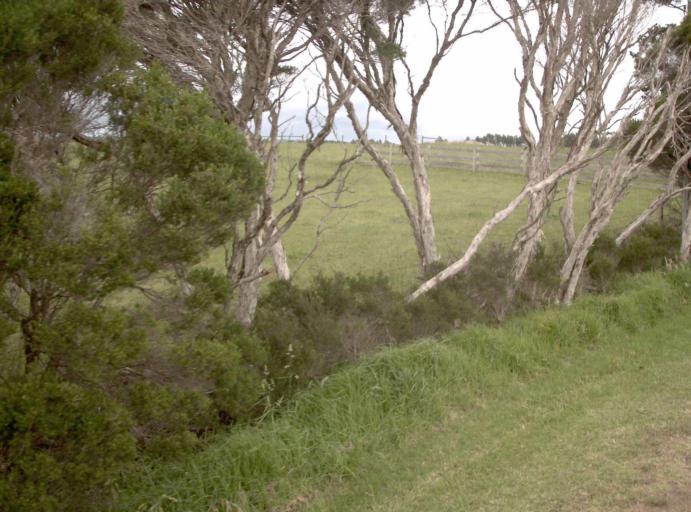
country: AU
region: Victoria
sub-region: Bass Coast
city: North Wonthaggi
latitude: -38.5511
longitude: 145.6745
